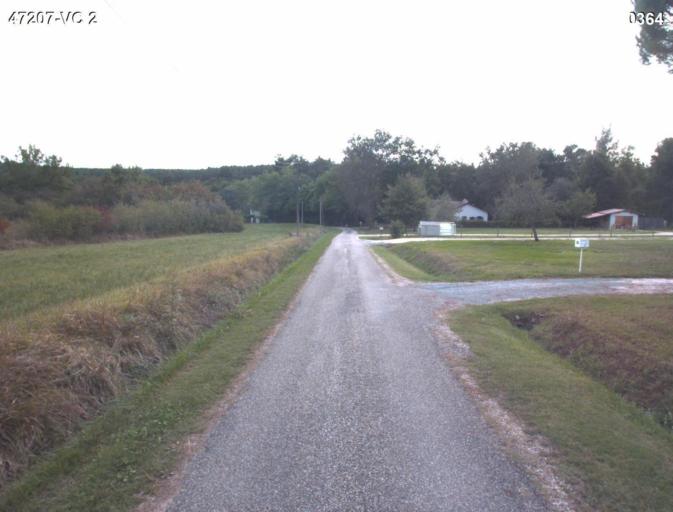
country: FR
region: Aquitaine
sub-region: Departement du Lot-et-Garonne
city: Barbaste
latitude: 44.1810
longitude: 0.2220
